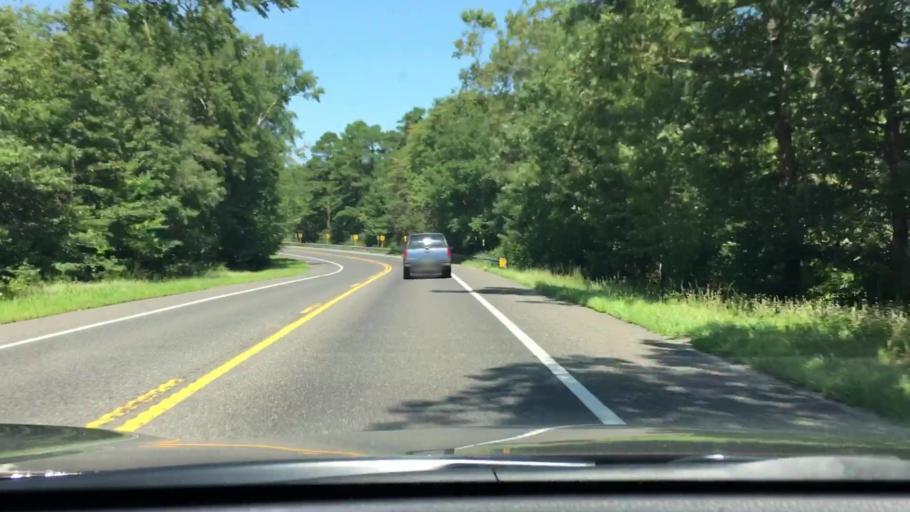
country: US
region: New Jersey
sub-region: Cumberland County
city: Port Norris
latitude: 39.2839
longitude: -74.9515
